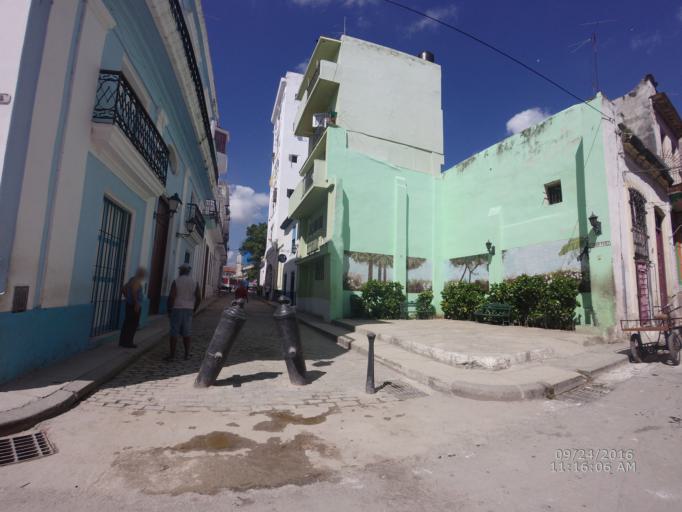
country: CU
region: La Habana
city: La Habana Vieja
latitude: 23.1300
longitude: -82.3530
